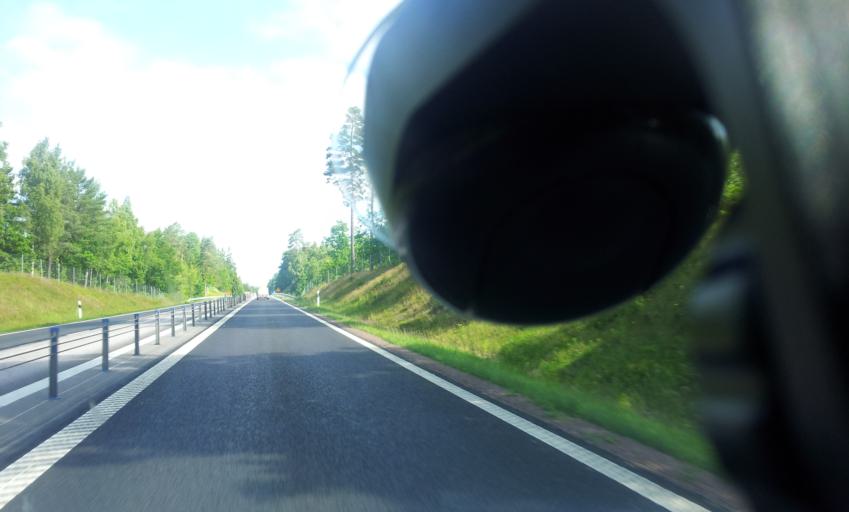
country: SE
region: Kalmar
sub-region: Monsteras Kommun
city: Timmernabben
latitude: 56.8864
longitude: 16.3823
